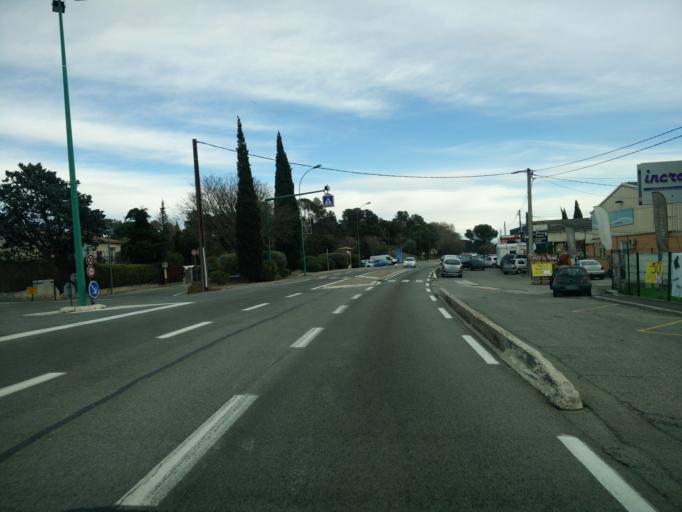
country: FR
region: Provence-Alpes-Cote d'Azur
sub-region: Departement du Var
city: Le Muy
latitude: 43.4702
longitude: 6.5803
